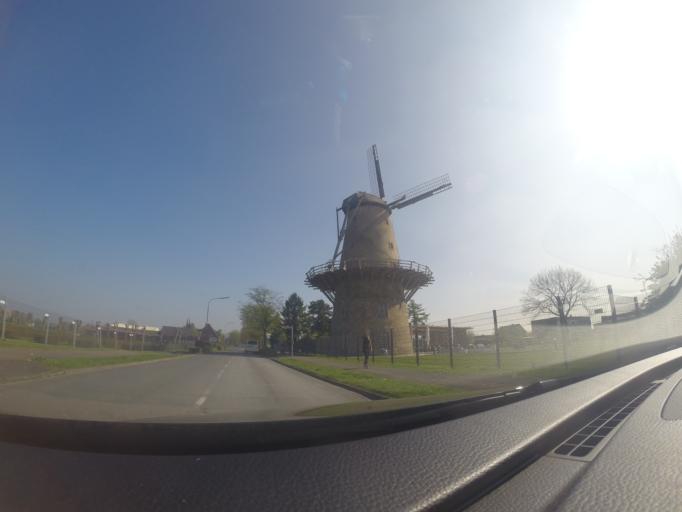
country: DE
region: North Rhine-Westphalia
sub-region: Regierungsbezirk Dusseldorf
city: Xanten
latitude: 51.6669
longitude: 6.4428
